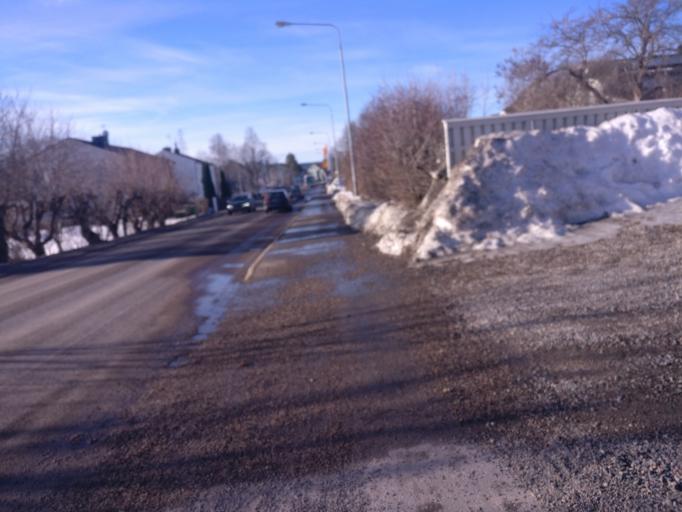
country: SE
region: Vaesternorrland
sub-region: Sundsvalls Kommun
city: Sundsvall
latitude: 62.4029
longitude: 17.3293
